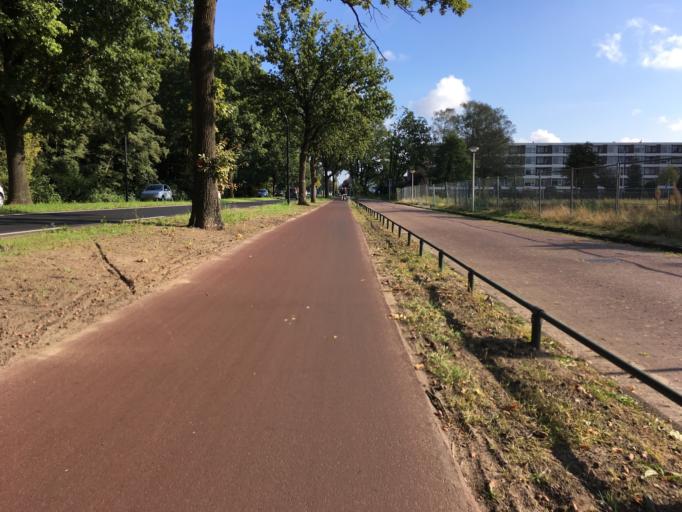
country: NL
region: Overijssel
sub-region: Gemeente Enschede
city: Enschede
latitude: 52.2323
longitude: 6.8647
